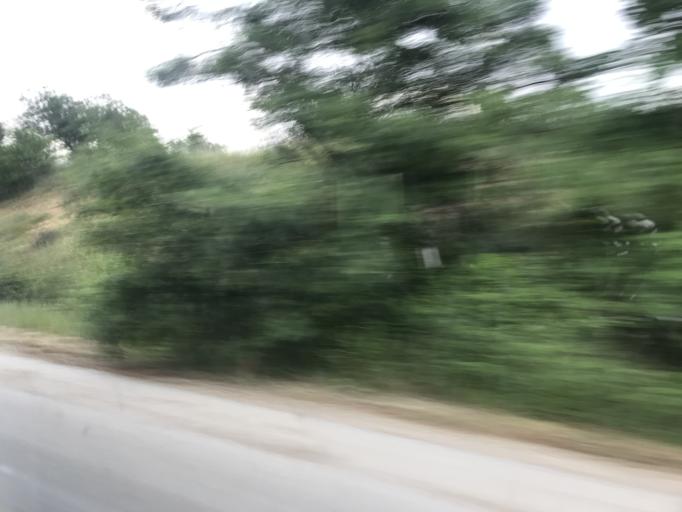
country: GR
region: East Macedonia and Thrace
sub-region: Nomos Rodopis
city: Sapes
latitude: 40.9973
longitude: 25.6621
